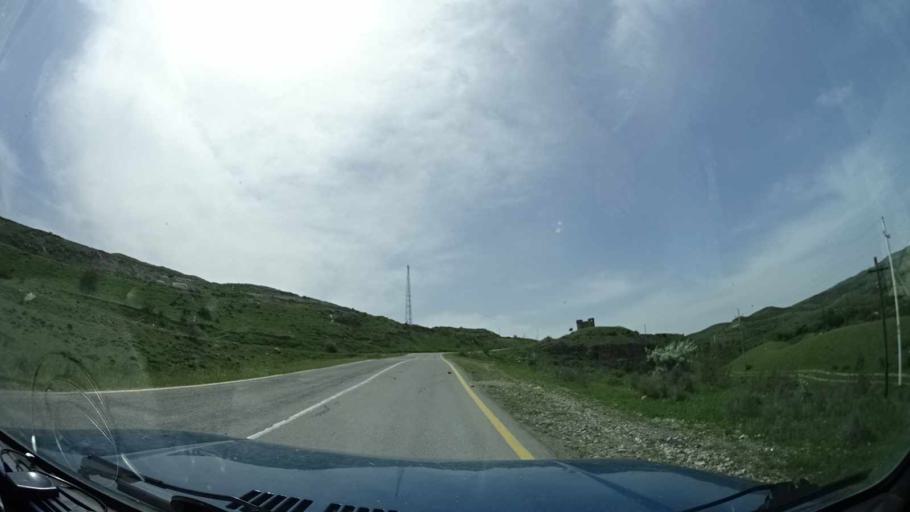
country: AZ
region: Xizi
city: Khyzy
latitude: 40.9043
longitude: 49.1148
